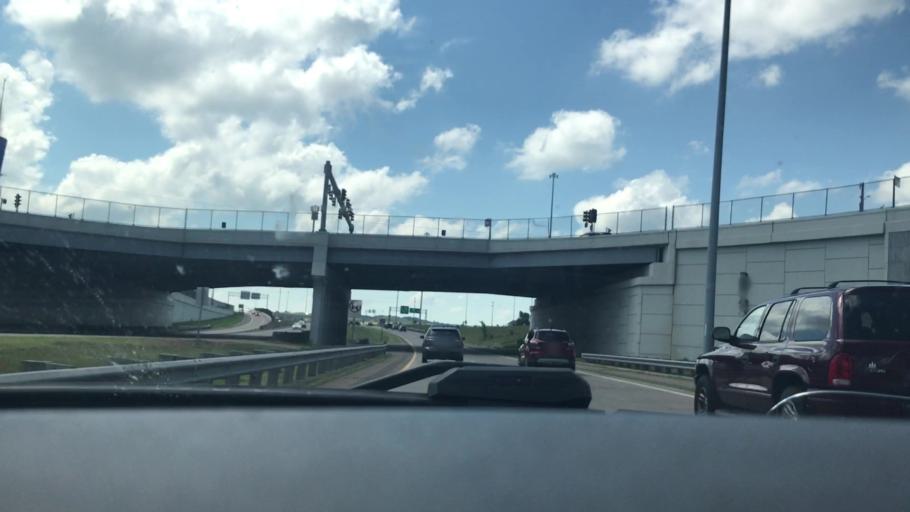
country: US
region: Wisconsin
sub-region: Eau Claire County
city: Altoona
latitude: 44.7959
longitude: -91.4561
